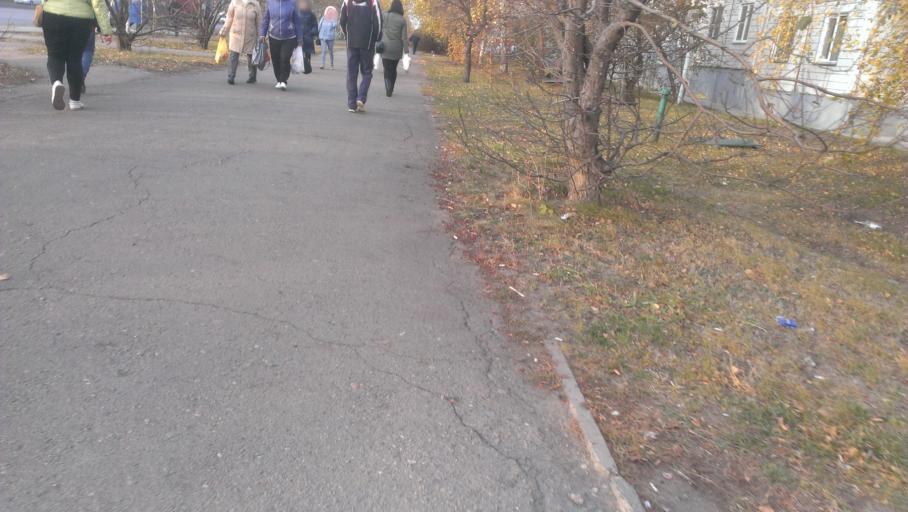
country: RU
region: Altai Krai
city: Novosilikatnyy
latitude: 53.3398
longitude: 83.6705
